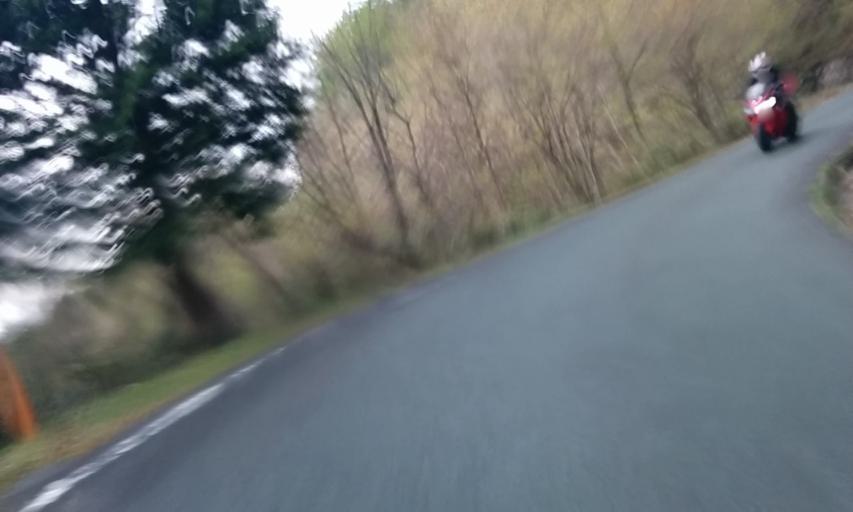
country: JP
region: Ehime
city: Saijo
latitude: 33.7864
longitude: 133.2802
